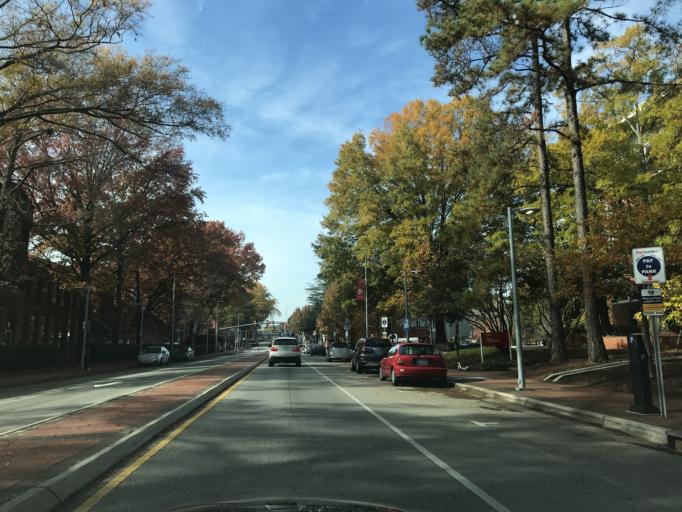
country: US
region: North Carolina
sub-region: Wake County
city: West Raleigh
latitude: 35.7869
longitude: -78.6645
